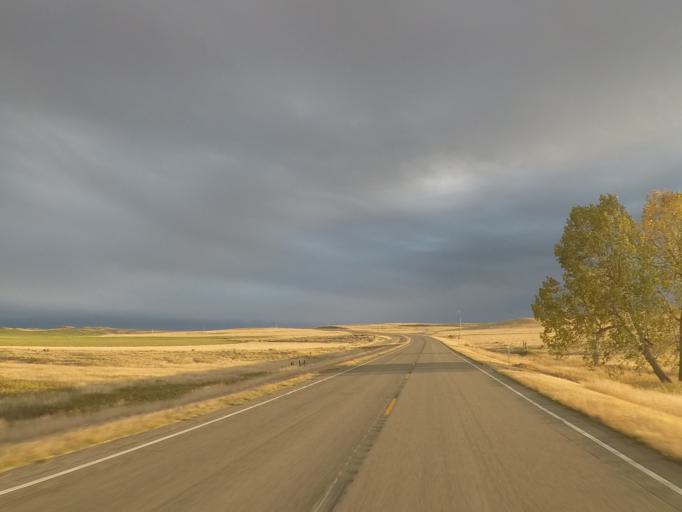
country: US
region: Montana
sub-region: Golden Valley County
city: Ryegate
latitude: 46.3617
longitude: -109.2681
